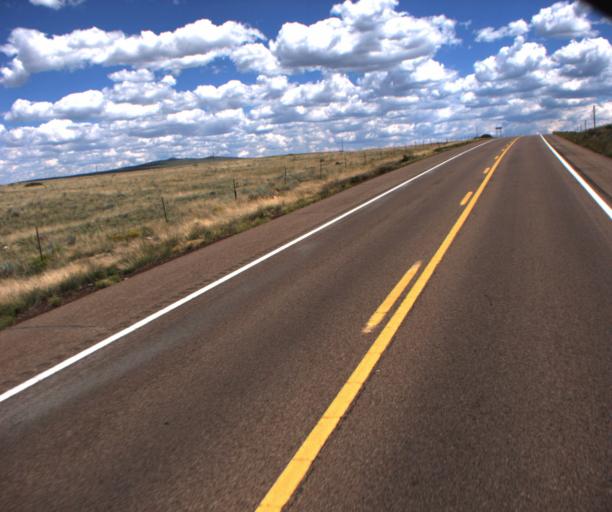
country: US
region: Arizona
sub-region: Apache County
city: Springerville
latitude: 34.1821
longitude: -109.3286
